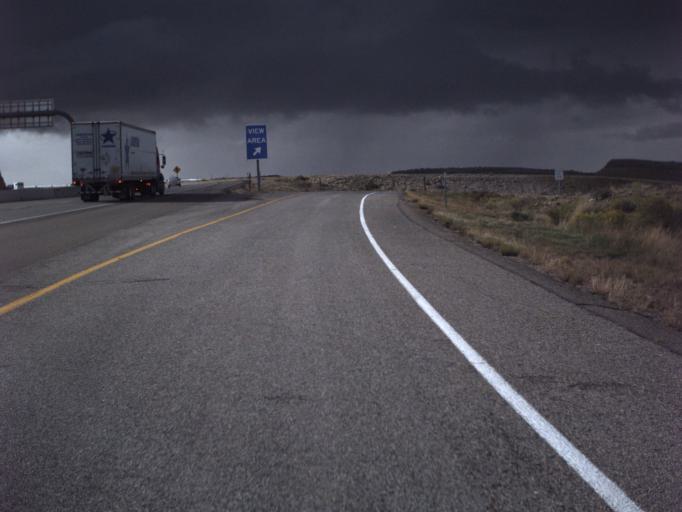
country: US
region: Utah
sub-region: Emery County
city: Castle Dale
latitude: 38.9371
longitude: -110.4786
